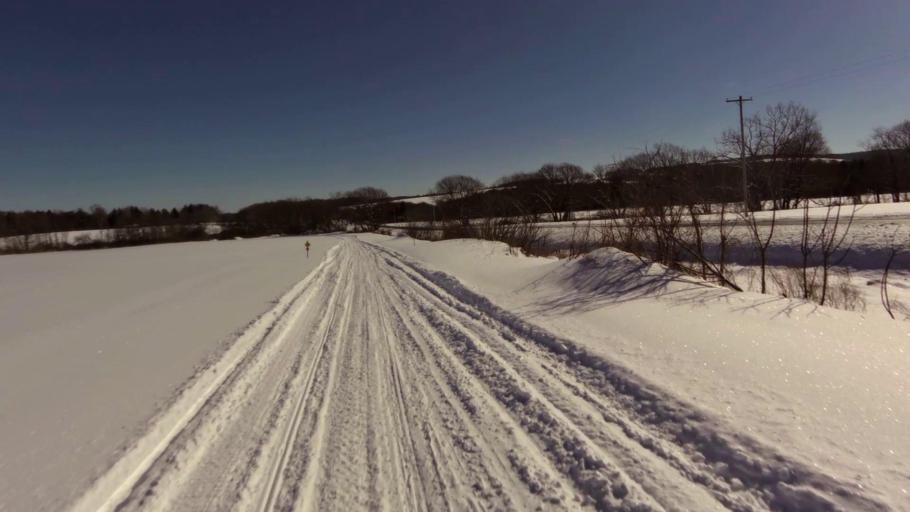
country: US
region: New York
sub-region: Chautauqua County
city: Fredonia
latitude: 42.3618
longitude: -79.1846
